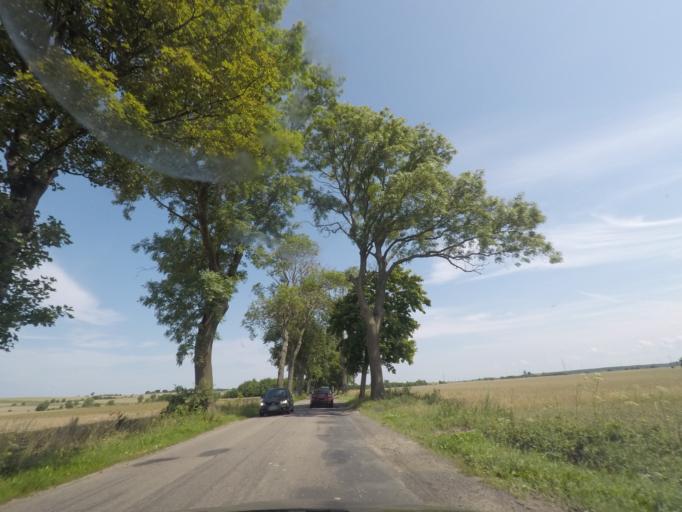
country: PL
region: West Pomeranian Voivodeship
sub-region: Powiat slawienski
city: Darlowo
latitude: 54.4409
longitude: 16.4470
